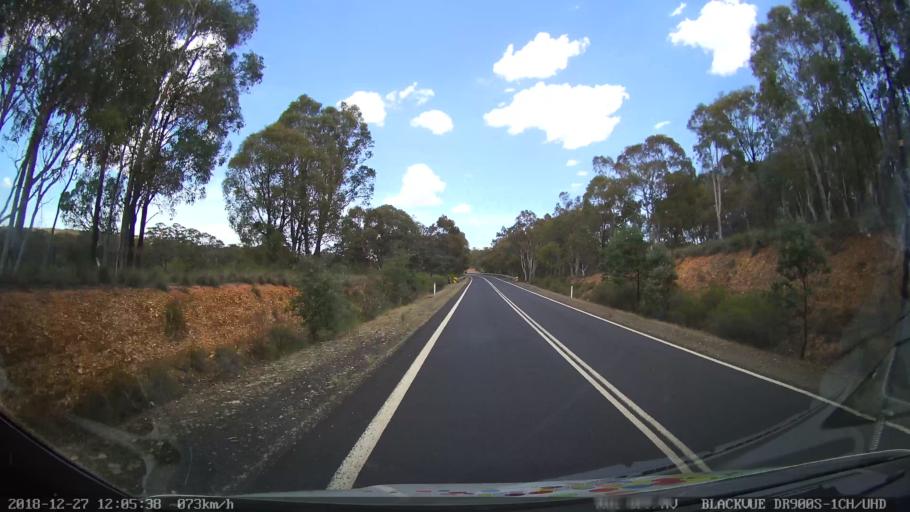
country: AU
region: New South Wales
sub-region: Blayney
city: Blayney
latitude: -33.8033
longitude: 149.3366
